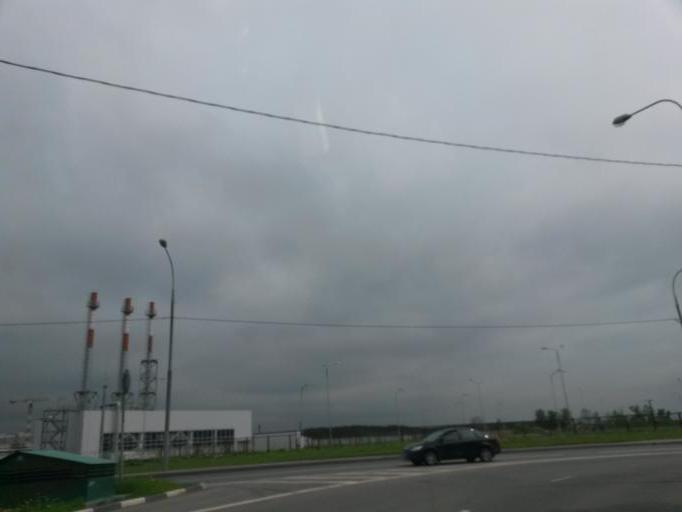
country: RU
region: Moskovskaya
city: Shcherbinka
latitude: 55.5182
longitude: 37.5771
